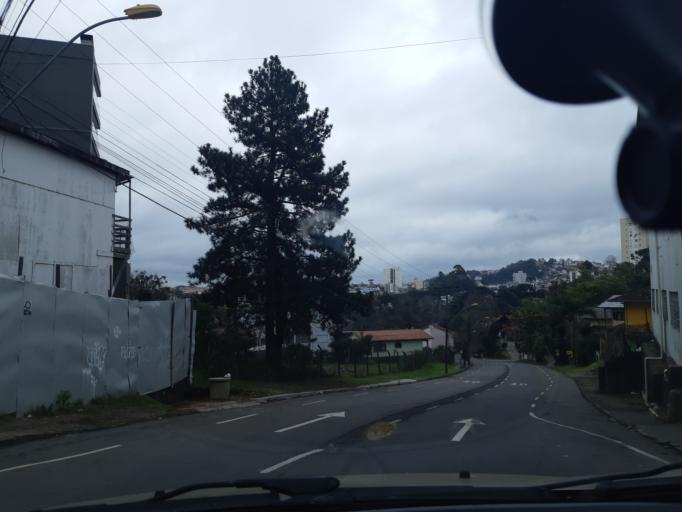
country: BR
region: Rio Grande do Sul
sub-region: Caxias Do Sul
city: Caxias do Sul
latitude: -29.1584
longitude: -51.1976
